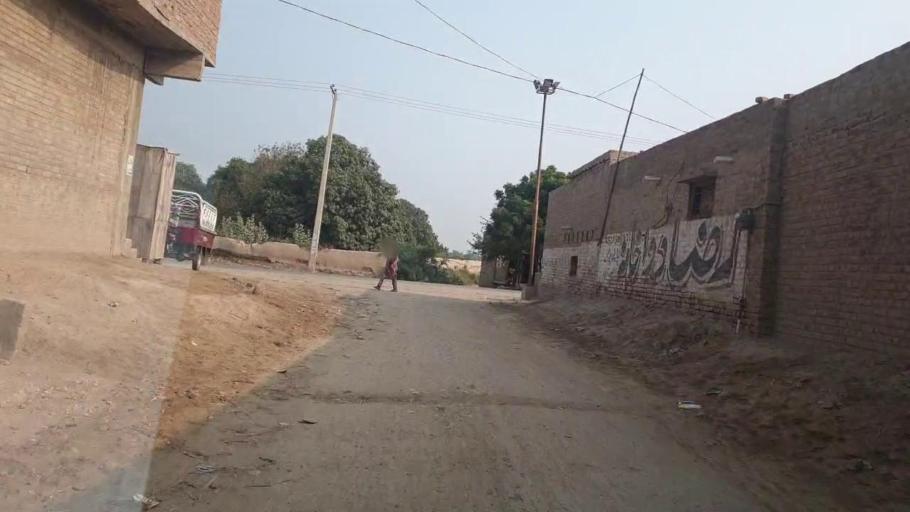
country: PK
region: Sindh
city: Tando Jam
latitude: 25.3394
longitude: 68.5239
